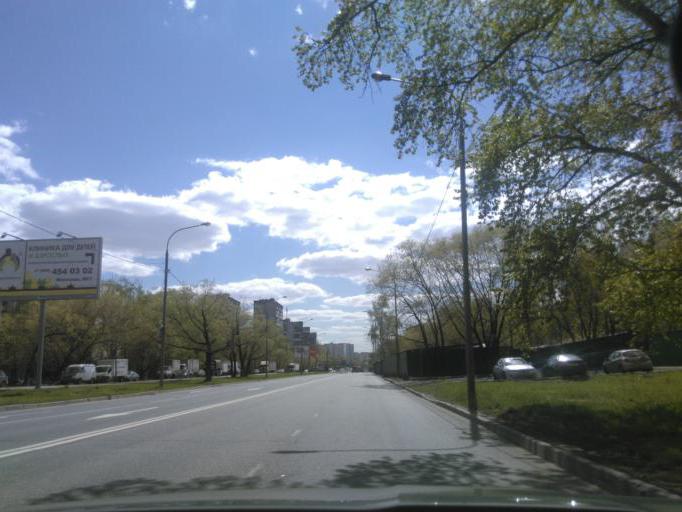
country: RU
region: Moscow
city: Novokhovrino
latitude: 55.8610
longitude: 37.5066
